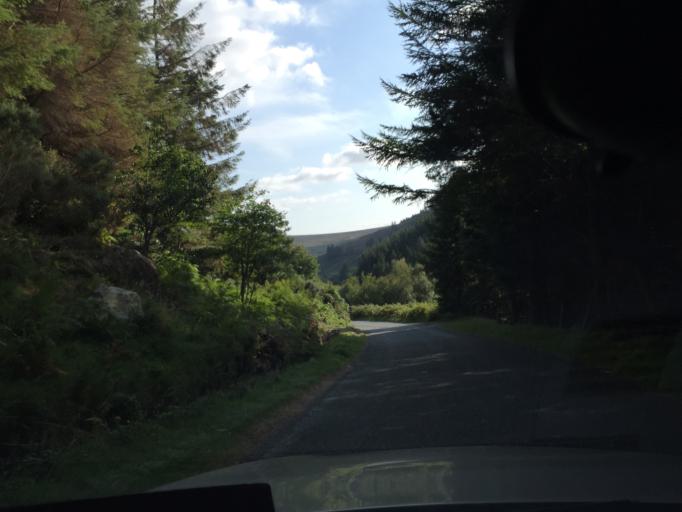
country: IE
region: Leinster
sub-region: Wicklow
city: Rathdrum
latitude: 53.0560
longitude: -6.3310
